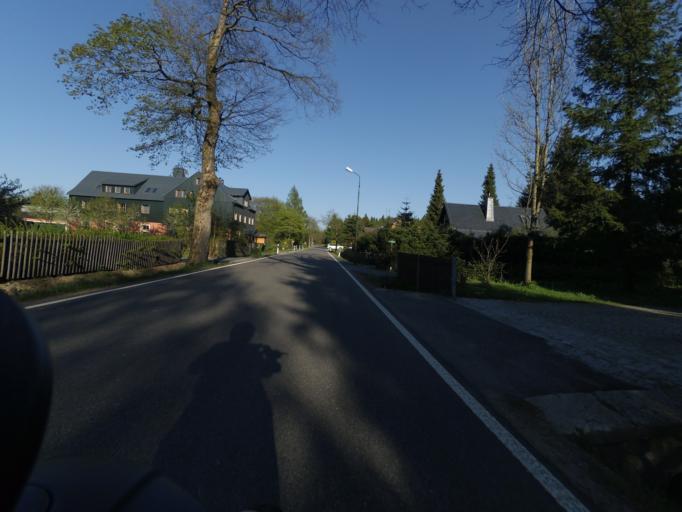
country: DE
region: Saxony
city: Altenberg
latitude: 50.7357
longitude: 13.6569
